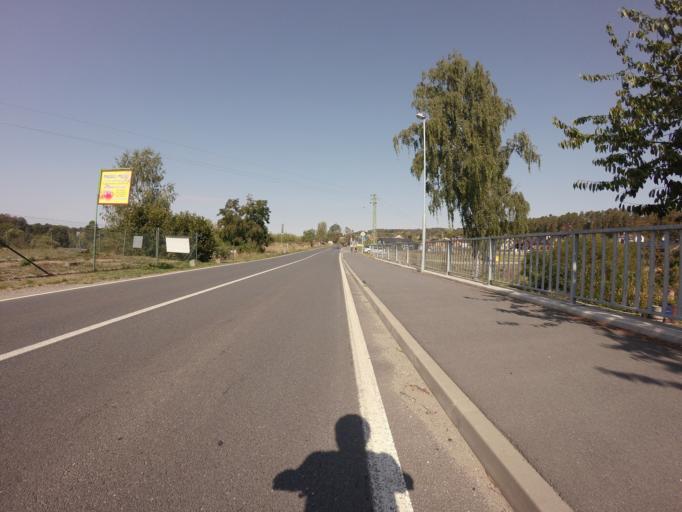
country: CZ
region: Central Bohemia
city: Tynec nad Sazavou
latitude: 49.8374
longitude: 14.5819
